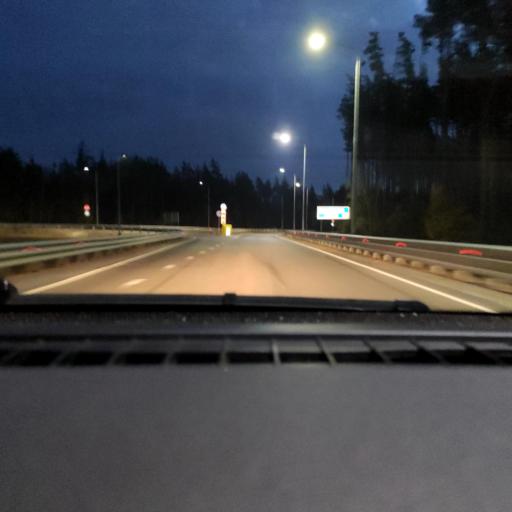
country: RU
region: Voronezj
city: Somovo
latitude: 51.6924
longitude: 39.3061
